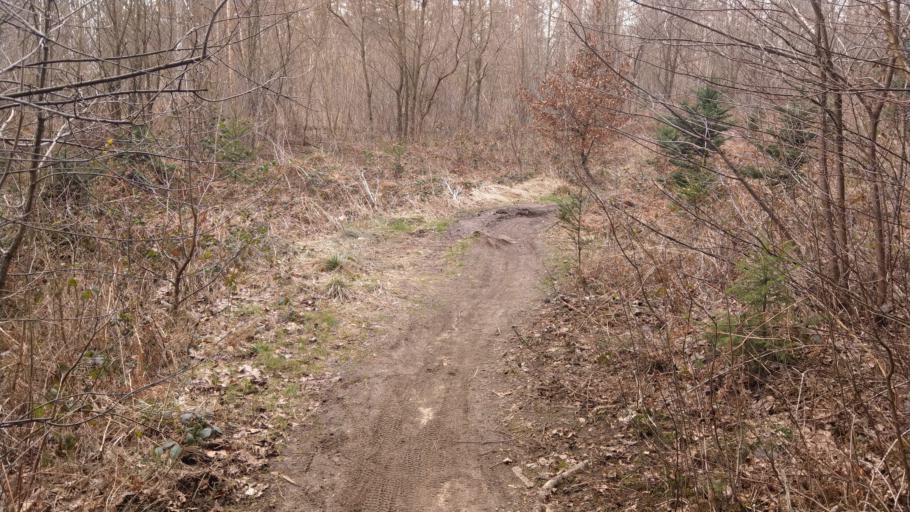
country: BE
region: Wallonia
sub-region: Province de Liege
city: La Calamine
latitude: 50.7364
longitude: 6.0067
